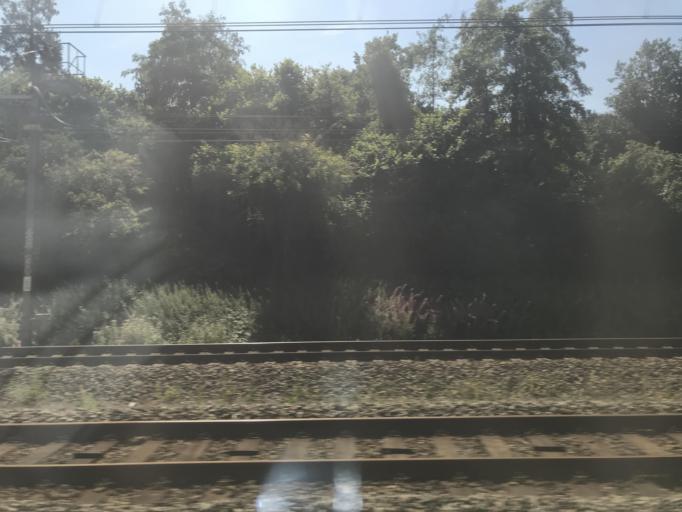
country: BE
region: Wallonia
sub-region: Province de Liege
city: Ans
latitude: 50.6608
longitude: 5.4971
